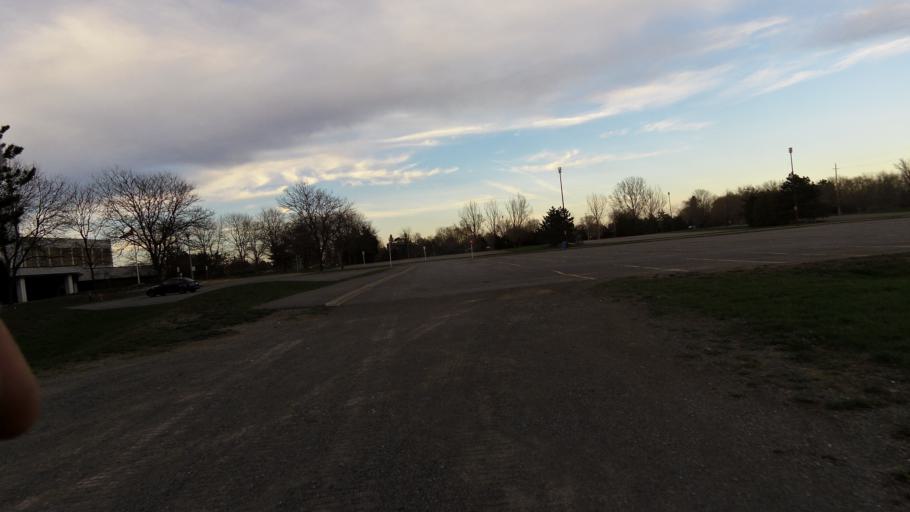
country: CA
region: Ontario
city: Bells Corners
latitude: 45.3430
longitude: -75.8391
